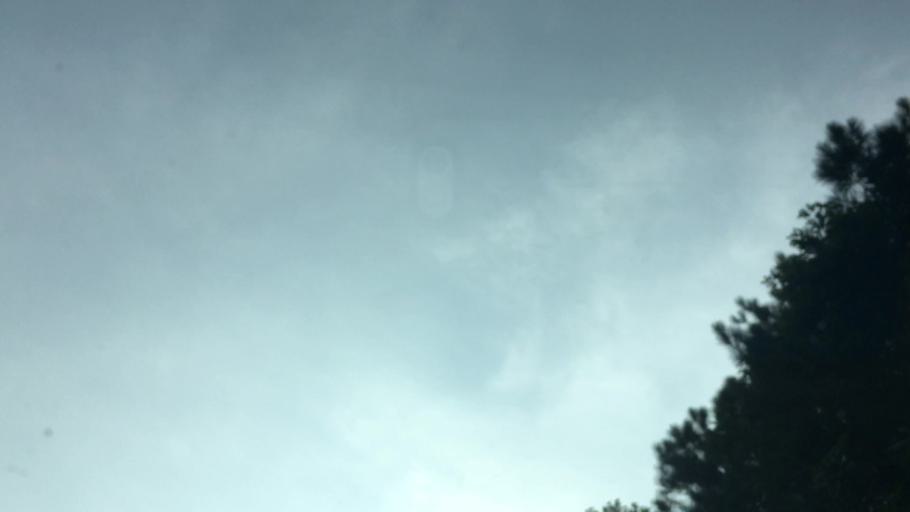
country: US
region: Alabama
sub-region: Bibb County
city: Woodstock
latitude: 33.2172
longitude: -87.0696
